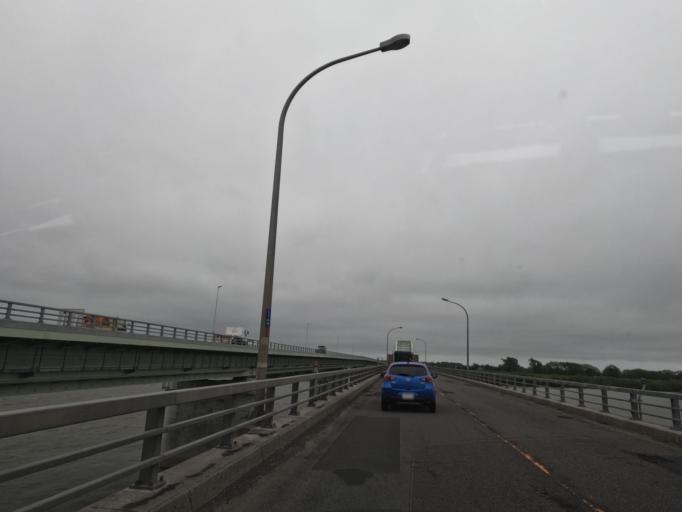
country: JP
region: Hokkaido
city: Ebetsu
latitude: 43.1338
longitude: 141.5098
